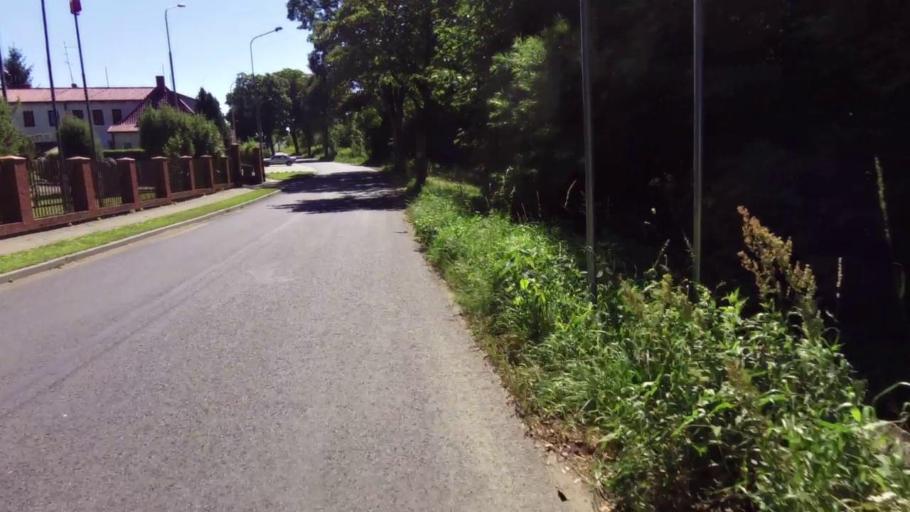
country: PL
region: West Pomeranian Voivodeship
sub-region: Powiat drawski
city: Czaplinek
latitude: 53.5623
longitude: 16.2453
